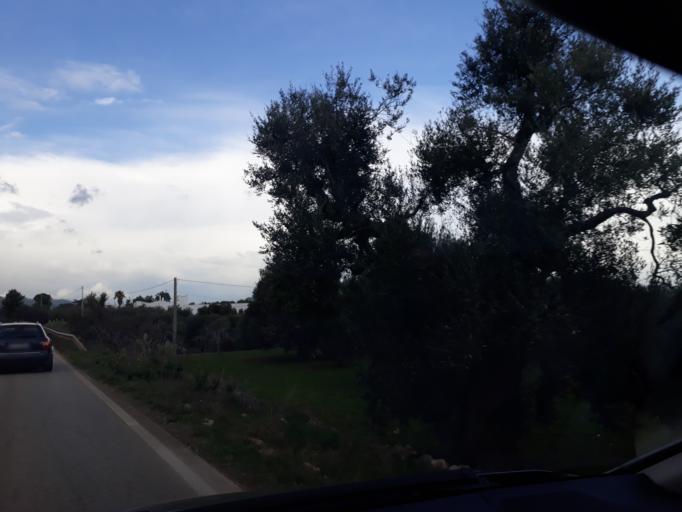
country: IT
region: Apulia
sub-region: Provincia di Brindisi
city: Pezze di Greco
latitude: 40.8009
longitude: 17.4015
